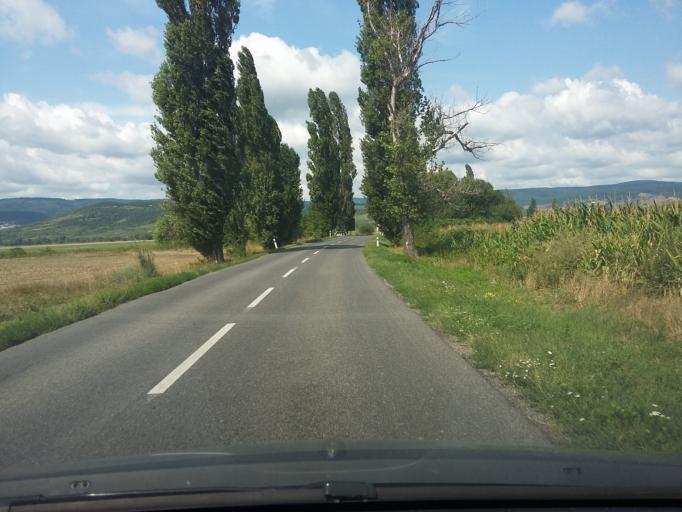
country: SK
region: Bratislavsky
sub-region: Okres Pezinok
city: Pezinok
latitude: 48.2574
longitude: 17.2615
